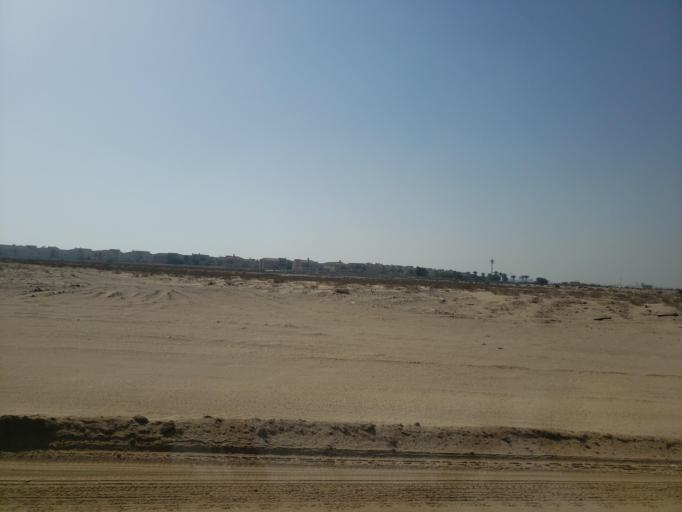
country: AE
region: Umm al Qaywayn
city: Umm al Qaywayn
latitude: 25.5298
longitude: 55.5920
